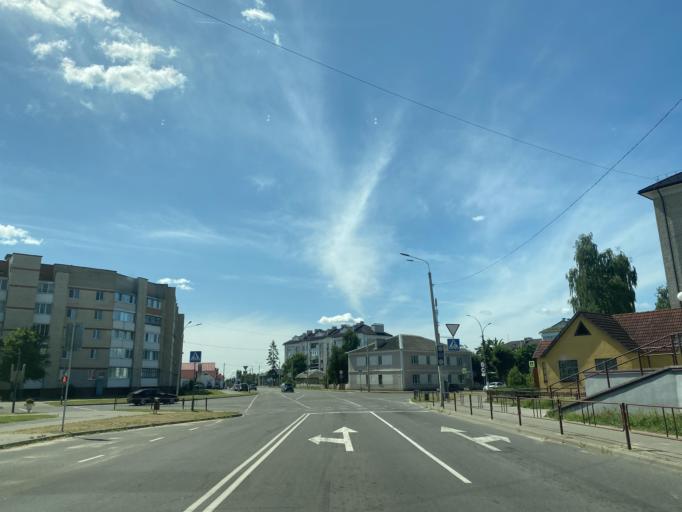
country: BY
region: Brest
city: Ivanava
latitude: 52.1494
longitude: 25.5420
